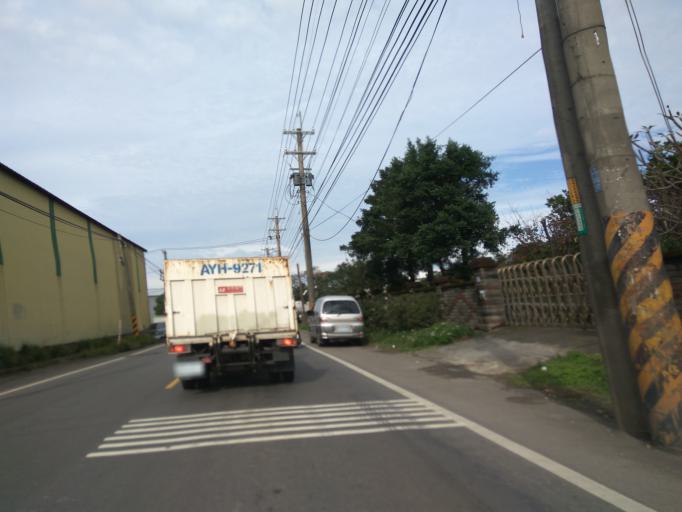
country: TW
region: Taiwan
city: Daxi
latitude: 24.9388
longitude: 121.1612
